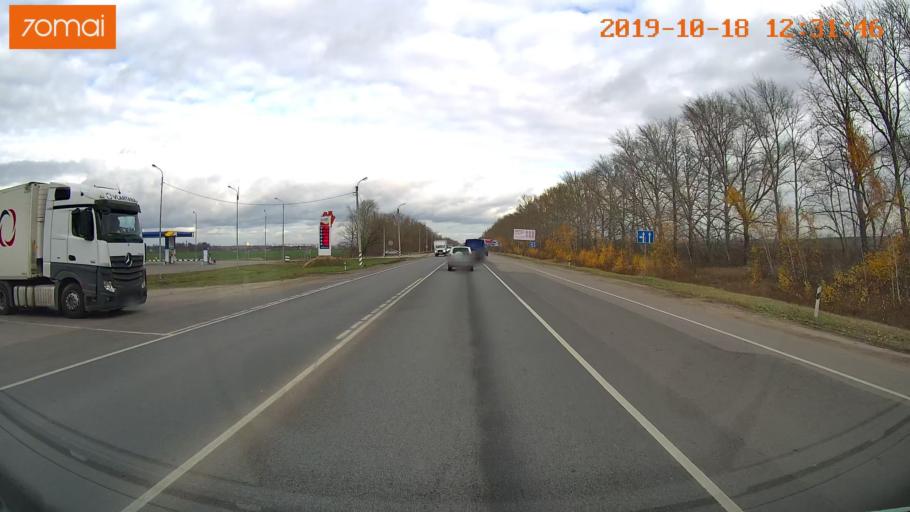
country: RU
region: Rjazan
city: Ryazan'
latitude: 54.5958
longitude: 39.6166
